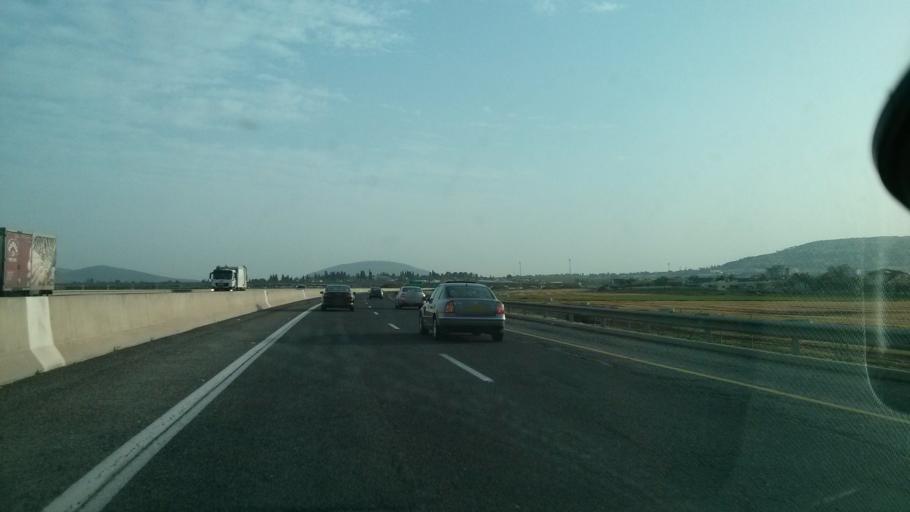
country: IL
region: Northern District
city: `Afula `Illit
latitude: 32.6190
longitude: 35.2786
